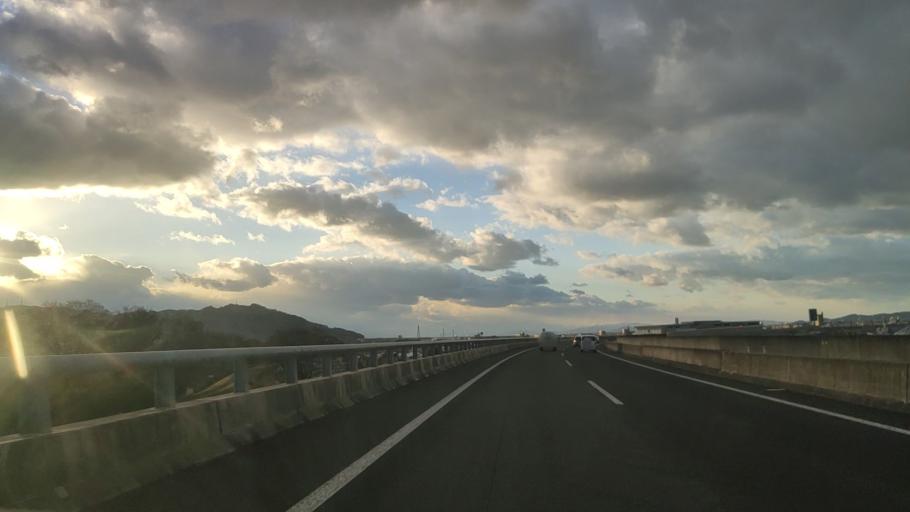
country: JP
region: Ehime
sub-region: Shikoku-chuo Shi
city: Matsuyama
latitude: 33.7877
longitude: 132.8099
